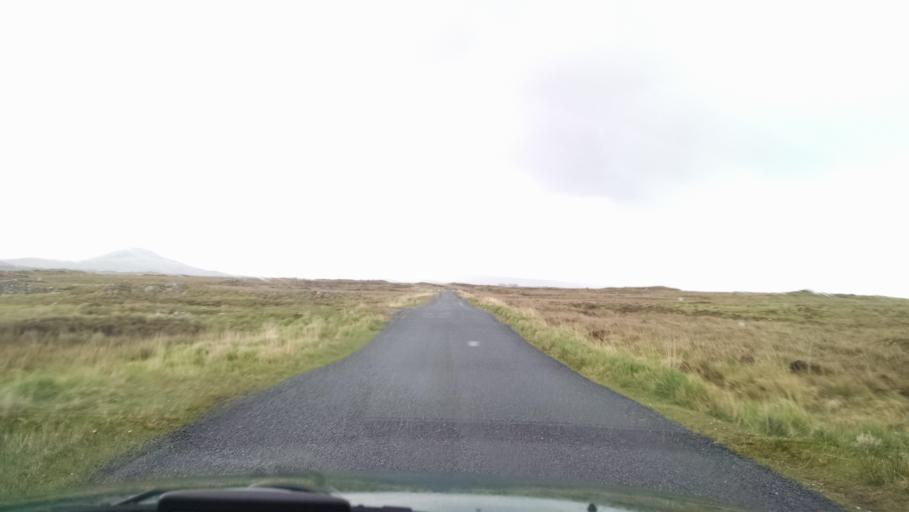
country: IE
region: Connaught
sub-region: County Galway
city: Clifden
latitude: 53.4389
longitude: -9.9193
